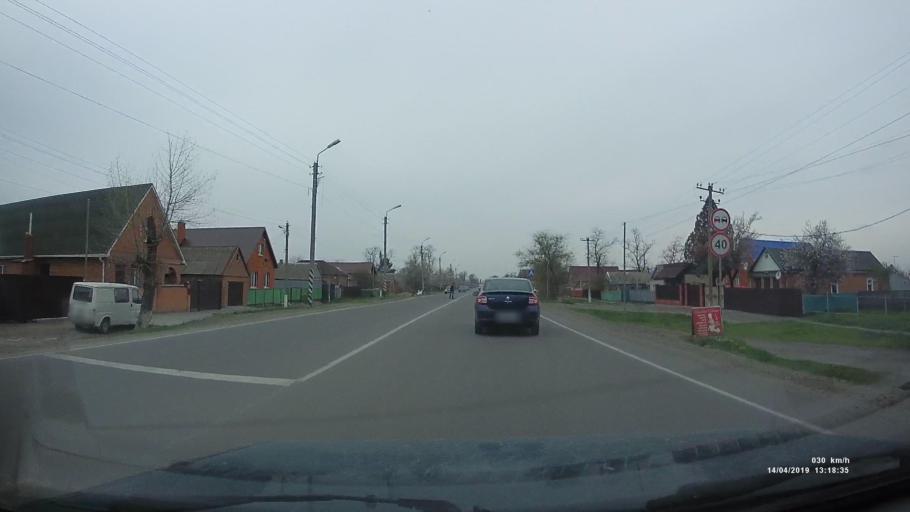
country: RU
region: Rostov
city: Kuleshovka
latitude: 47.0786
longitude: 39.5548
